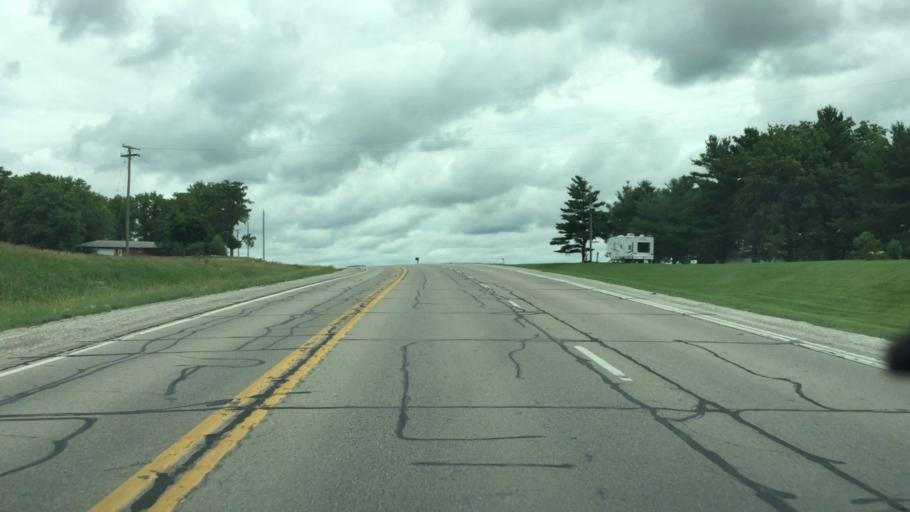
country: US
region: Iowa
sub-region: Jasper County
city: Monroe
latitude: 41.5453
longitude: -93.0976
